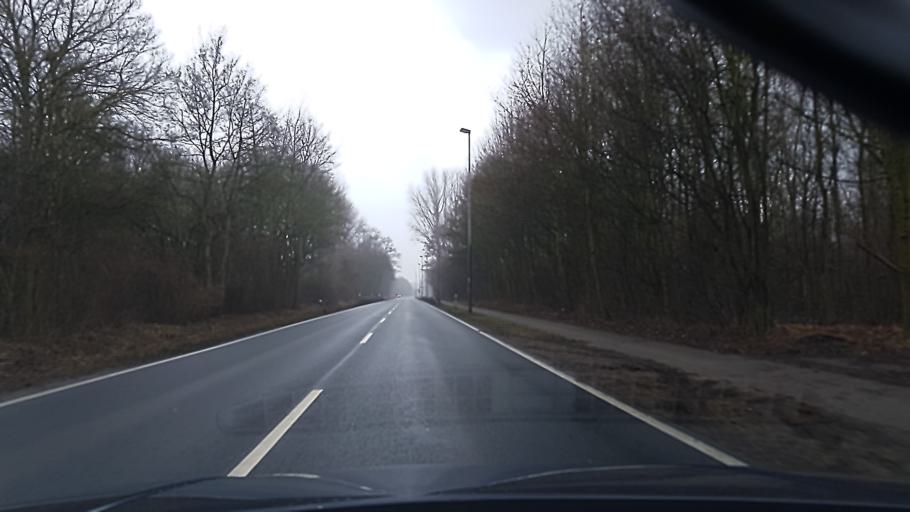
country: DE
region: Lower Saxony
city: Cramme
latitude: 52.1590
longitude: 10.4272
